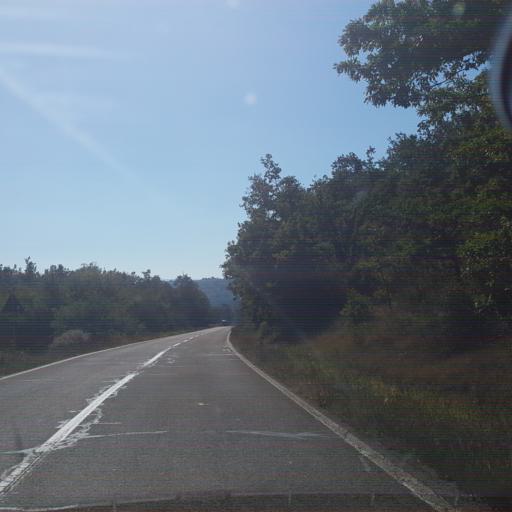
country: RS
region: Central Serbia
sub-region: Nisavski Okrug
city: Svrljig
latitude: 43.4598
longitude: 22.2075
